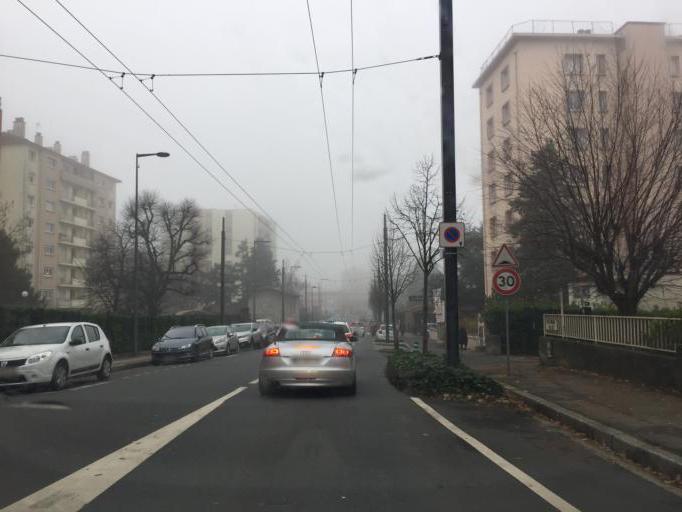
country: FR
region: Rhone-Alpes
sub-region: Departement du Rhone
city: Caluire-et-Cuire
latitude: 45.7894
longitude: 4.8407
